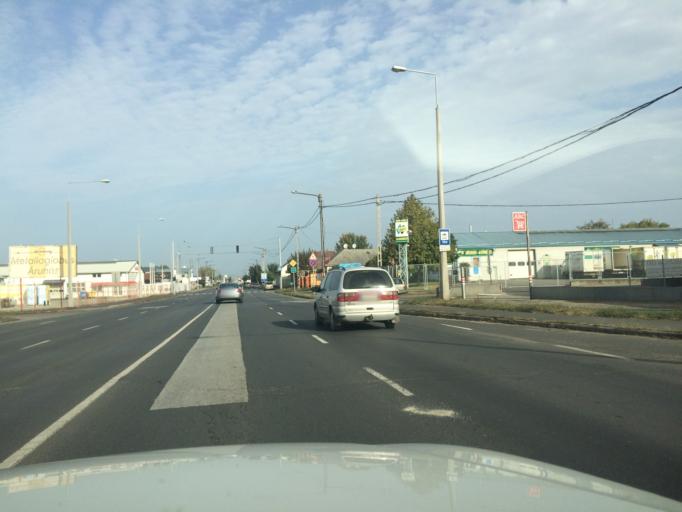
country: HU
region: Szabolcs-Szatmar-Bereg
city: Nyiregyhaza
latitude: 47.9196
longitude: 21.7194
